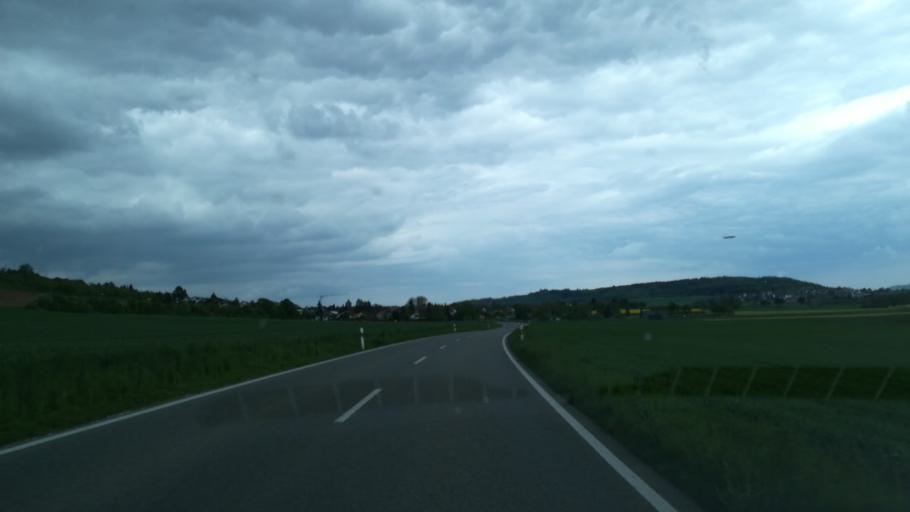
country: CH
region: Schaffhausen
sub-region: Bezirk Reiat
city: Thayngen
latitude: 47.7673
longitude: 8.7360
